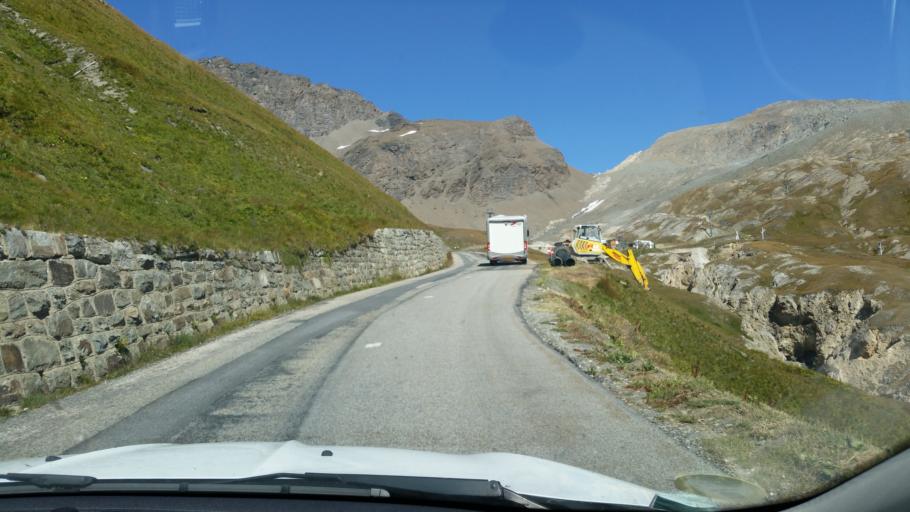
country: FR
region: Rhone-Alpes
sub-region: Departement de la Savoie
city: Val-d'Isere
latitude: 45.4183
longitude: 7.0354
